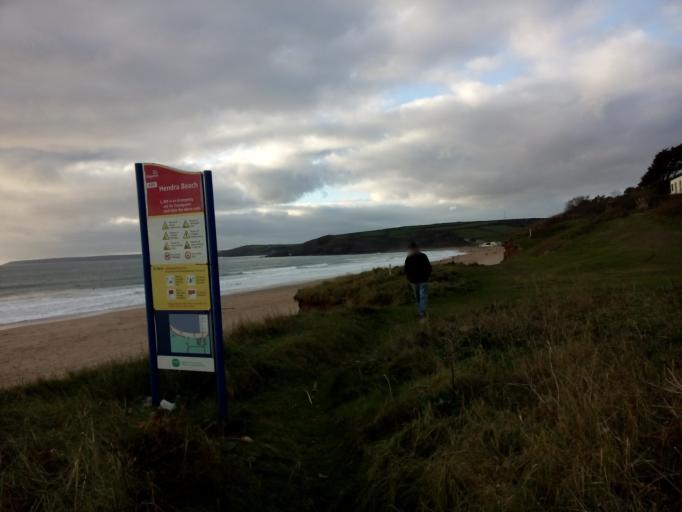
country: GB
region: England
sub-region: Cornwall
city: Germoe
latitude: 50.0995
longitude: -5.3776
